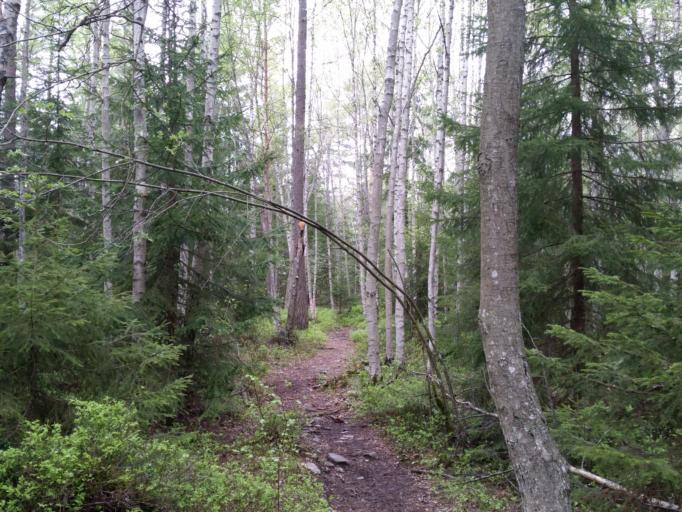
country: SE
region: Stockholm
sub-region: Sollentuna Kommun
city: Sollentuna
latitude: 59.4683
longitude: 17.9498
